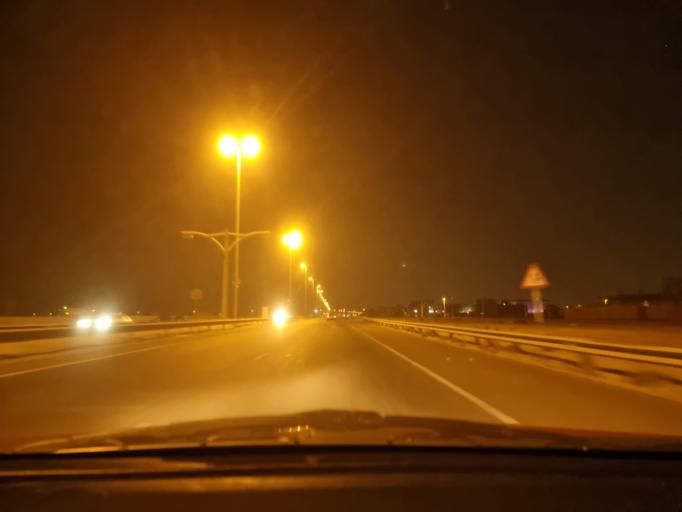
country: AE
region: Abu Dhabi
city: Abu Dhabi
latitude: 24.3709
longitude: 54.6722
